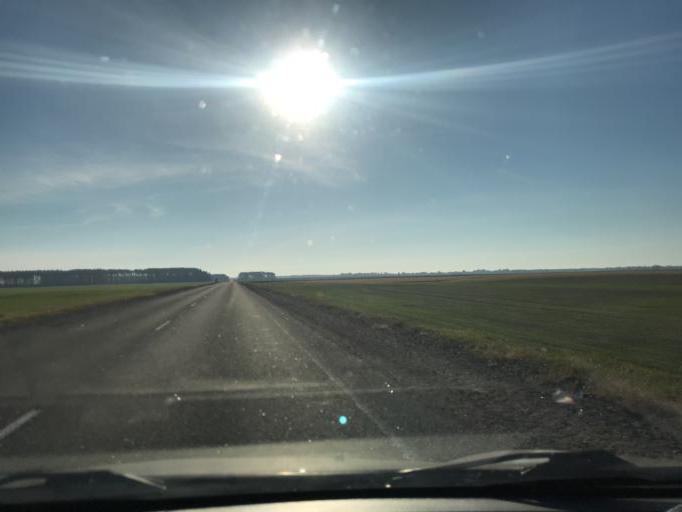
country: BY
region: Gomel
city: Khoyniki
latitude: 51.8233
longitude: 30.0748
